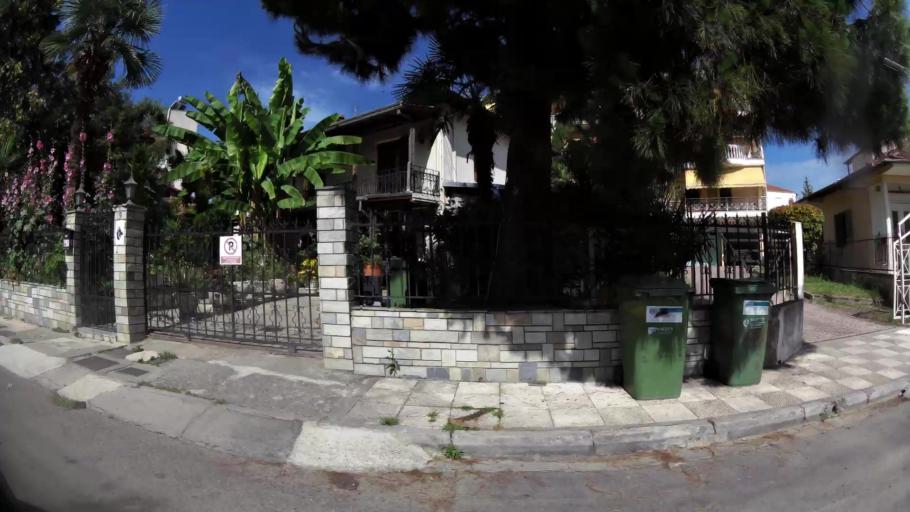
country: GR
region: Central Macedonia
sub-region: Nomos Pierias
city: Katerini
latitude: 40.2783
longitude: 22.5058
